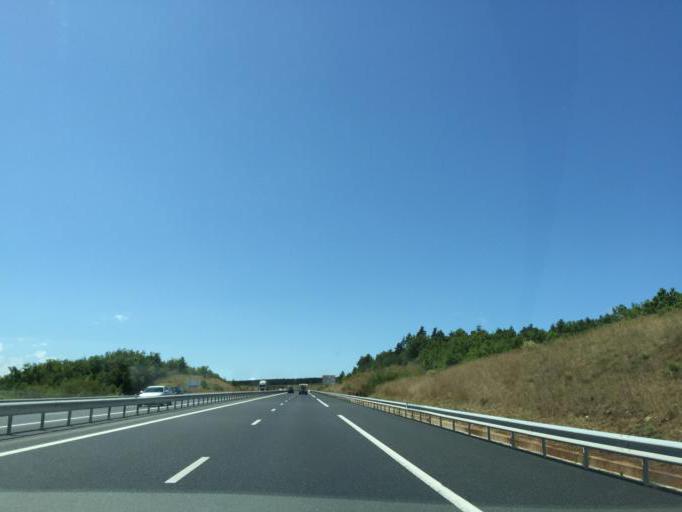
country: FR
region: Midi-Pyrenees
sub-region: Departement de l'Aveyron
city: Millau
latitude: 44.1851
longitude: 3.0502
